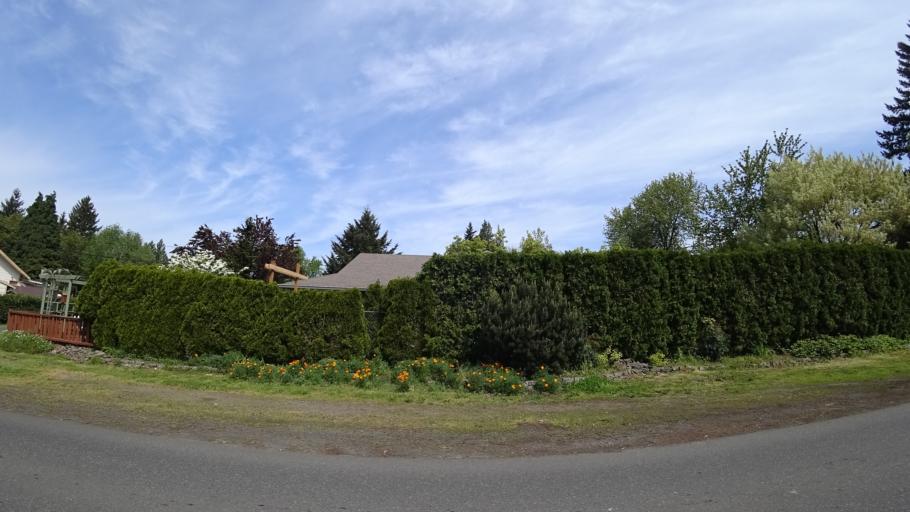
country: US
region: Oregon
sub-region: Clackamas County
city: Milwaukie
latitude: 45.4451
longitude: -122.6116
